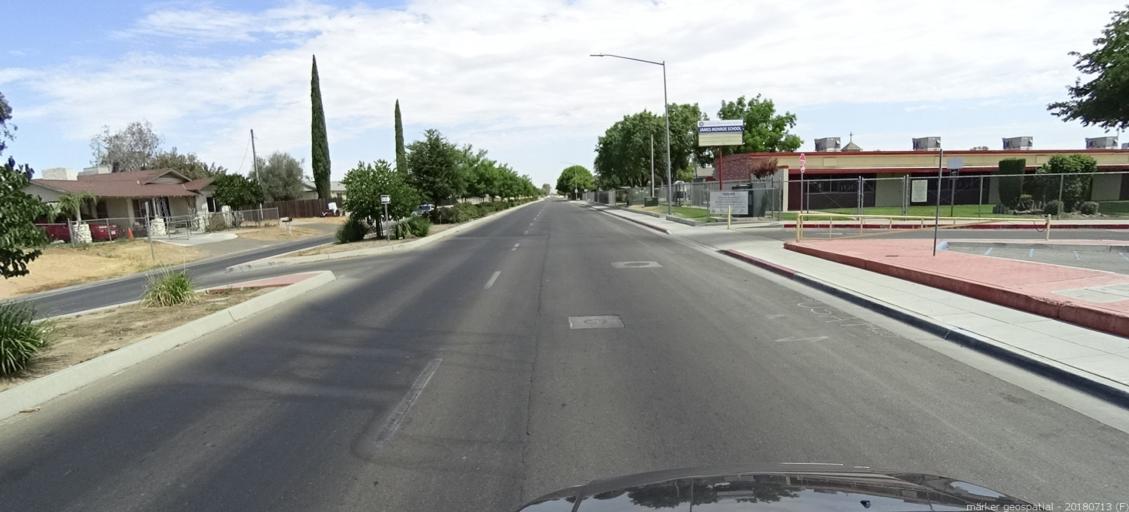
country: US
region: California
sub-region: Madera County
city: Madera
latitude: 36.9837
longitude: -120.0561
